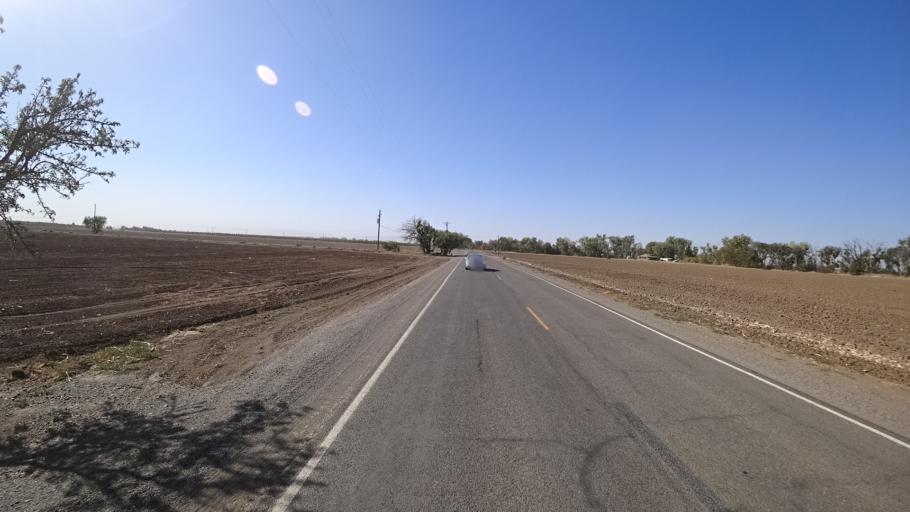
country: US
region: California
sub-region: Yolo County
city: Davis
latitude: 38.5904
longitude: -121.7960
